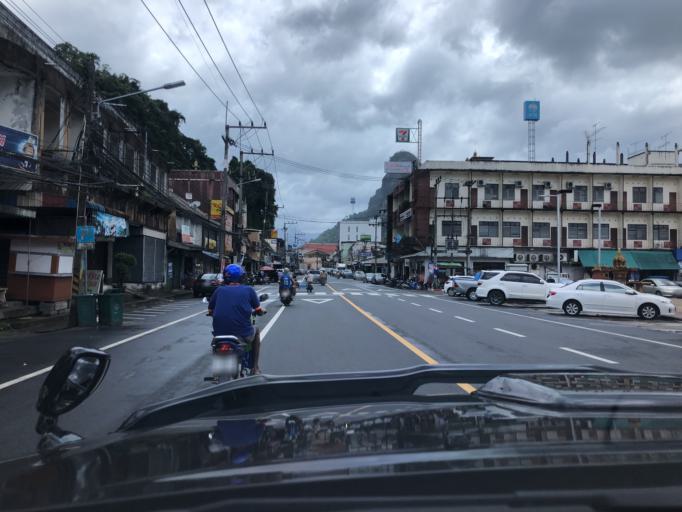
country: TH
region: Phangnga
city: Phang Nga
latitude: 8.4650
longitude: 98.5312
